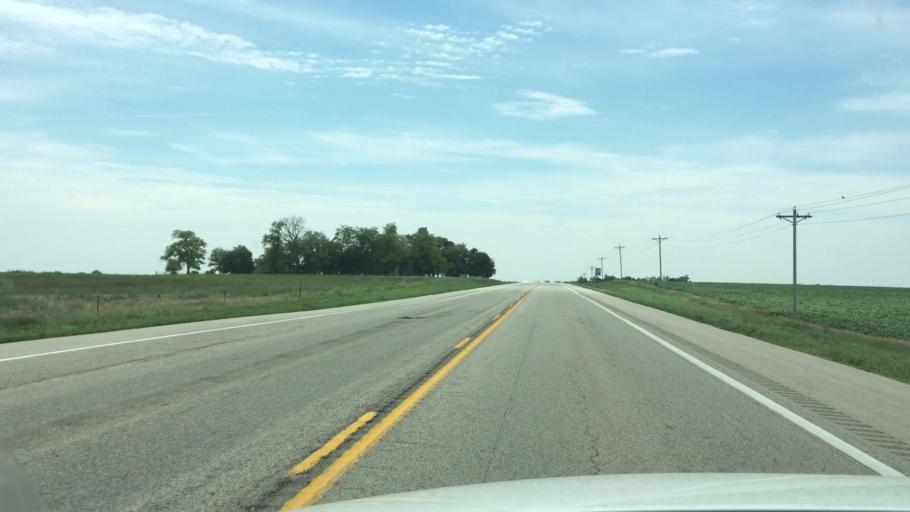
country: US
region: Kansas
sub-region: Nemaha County
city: Sabetha
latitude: 39.7532
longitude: -95.7297
